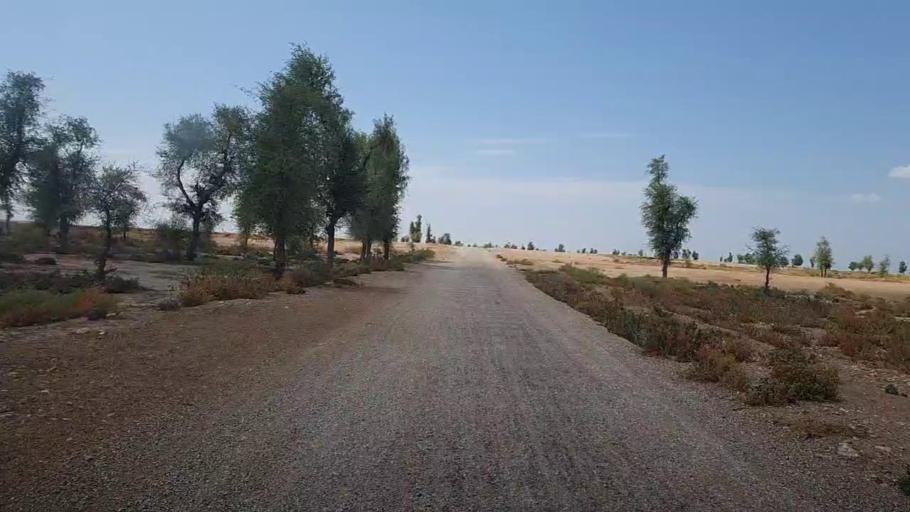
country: PK
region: Sindh
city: Sehwan
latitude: 26.3305
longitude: 67.6793
